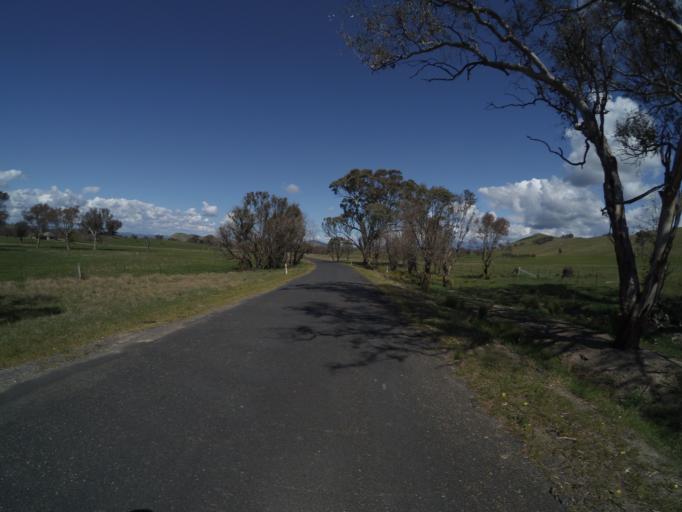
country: AU
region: New South Wales
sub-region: Yass Valley
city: Murrumbateman
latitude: -35.0950
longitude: 148.8524
